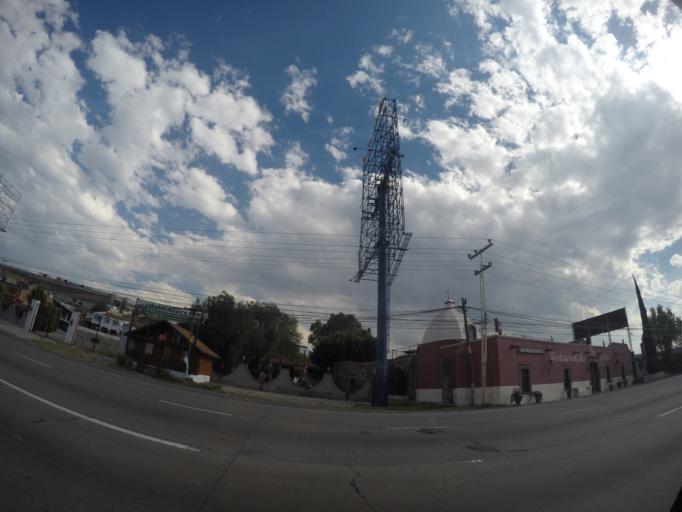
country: MX
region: Queretaro
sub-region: El Marques
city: General Lazaro Cardenas (El Colorado)
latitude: 20.5632
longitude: -100.2396
